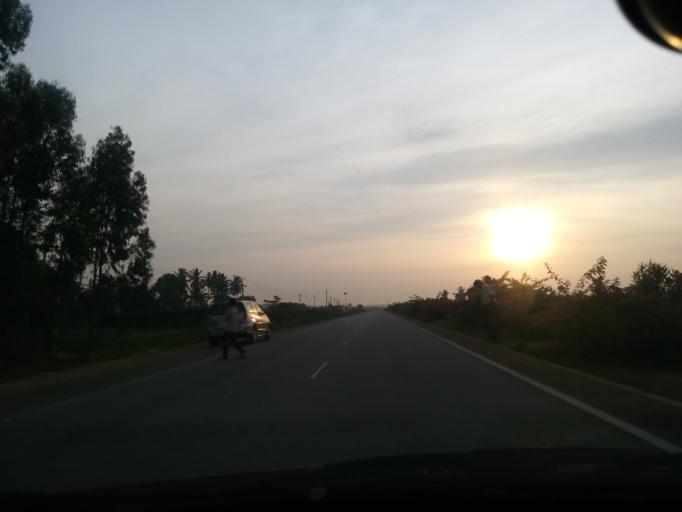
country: IN
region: Karnataka
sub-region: Chikkaballapur
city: Chik Ballapur
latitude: 13.3879
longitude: 77.7332
